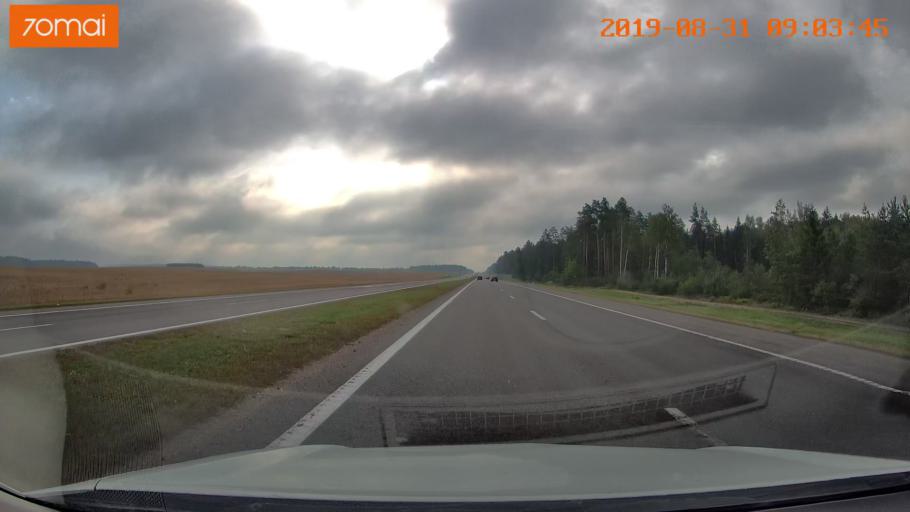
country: BY
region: Minsk
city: Chervyen'
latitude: 53.7377
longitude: 28.3265
